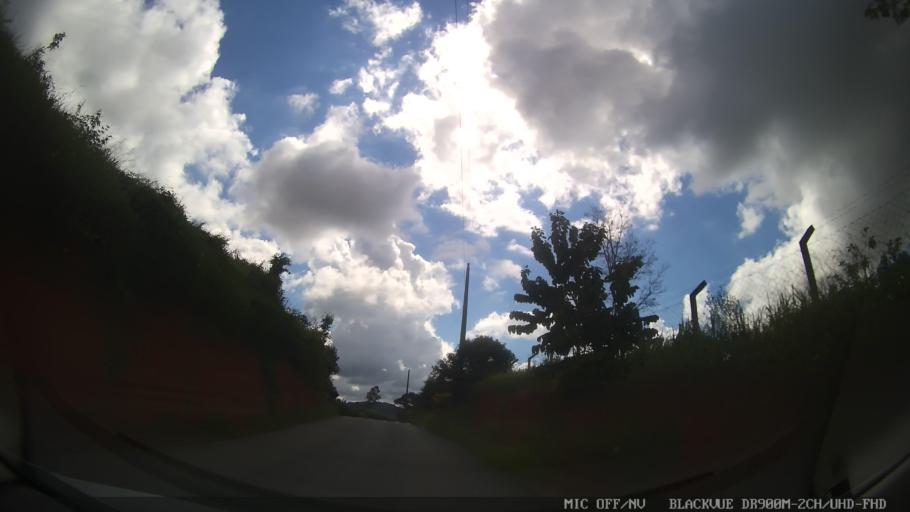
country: BR
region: Sao Paulo
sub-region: Braganca Paulista
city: Braganca Paulista
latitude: -22.9167
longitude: -46.4393
